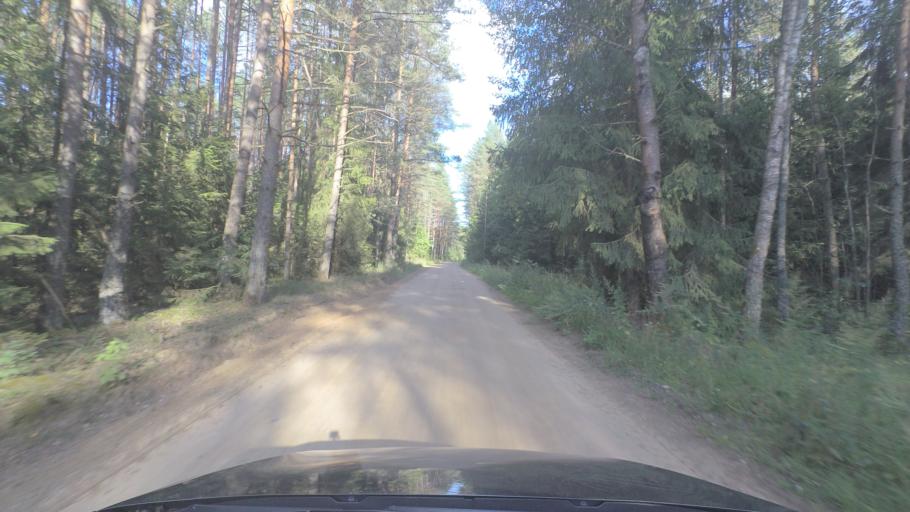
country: LT
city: Pabrade
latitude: 55.1484
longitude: 25.7511
